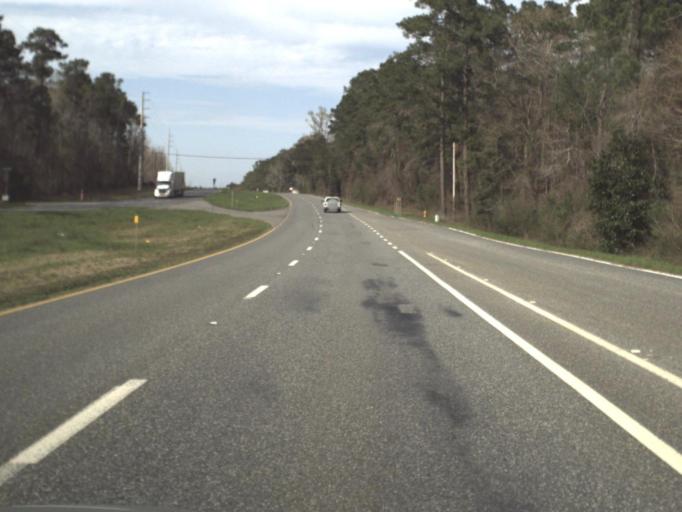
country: US
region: Florida
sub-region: Jefferson County
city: Monticello
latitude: 30.4570
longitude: -83.8930
